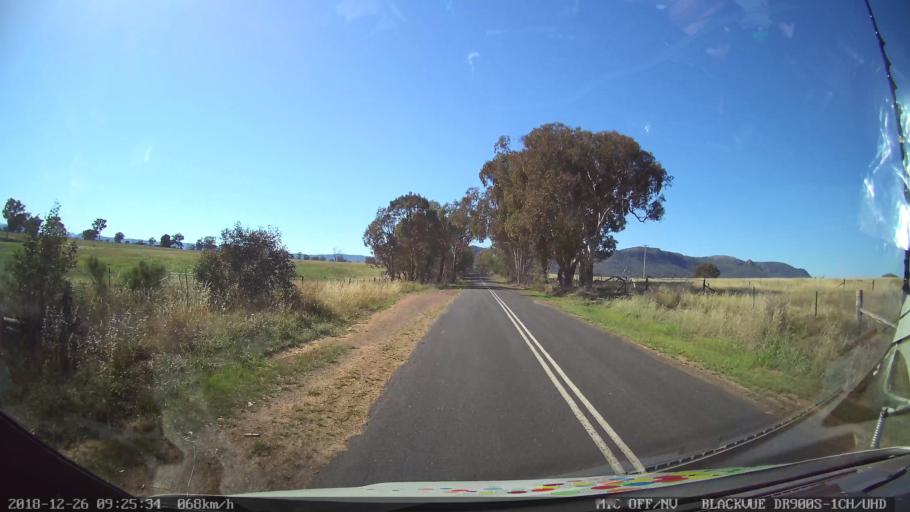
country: AU
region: New South Wales
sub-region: Mid-Western Regional
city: Kandos
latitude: -32.8211
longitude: 150.0042
